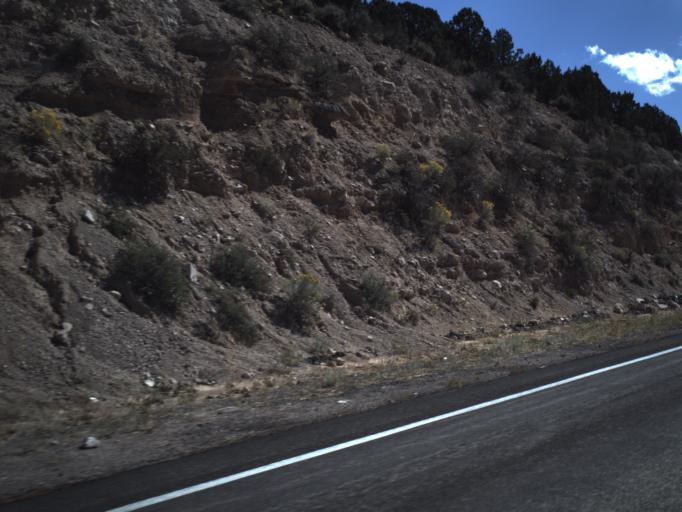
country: US
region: Utah
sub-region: Washington County
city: Enterprise
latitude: 37.5532
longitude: -113.6879
